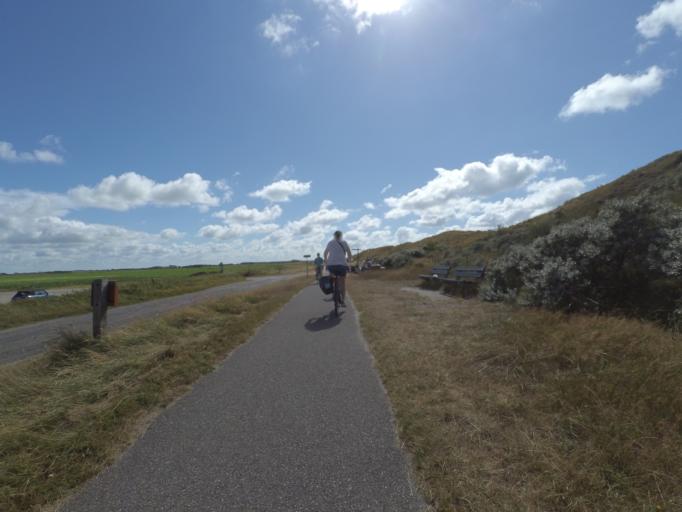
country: NL
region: North Holland
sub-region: Gemeente Texel
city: Den Burg
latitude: 53.1198
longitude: 4.8037
